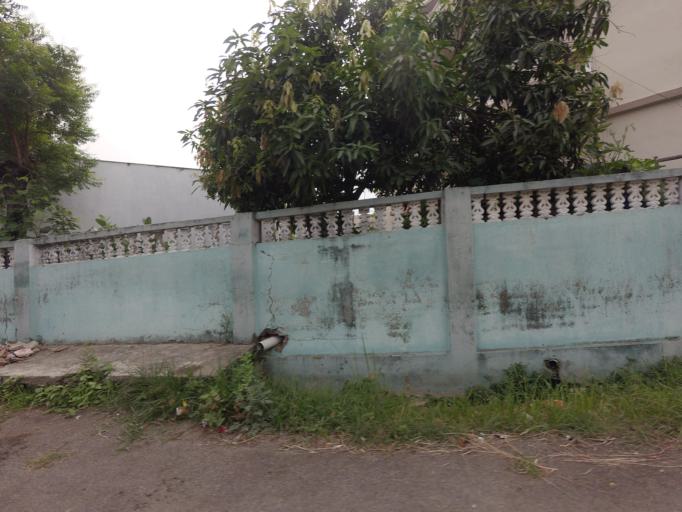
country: NP
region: Western Region
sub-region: Lumbini Zone
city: Bhairahawa
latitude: 27.5246
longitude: 83.4528
